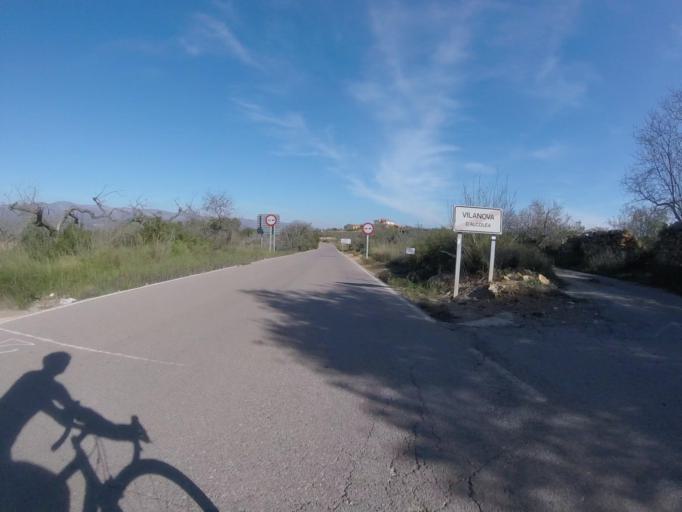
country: ES
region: Valencia
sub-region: Provincia de Castello
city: Benlloch
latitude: 40.2354
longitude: 0.0739
